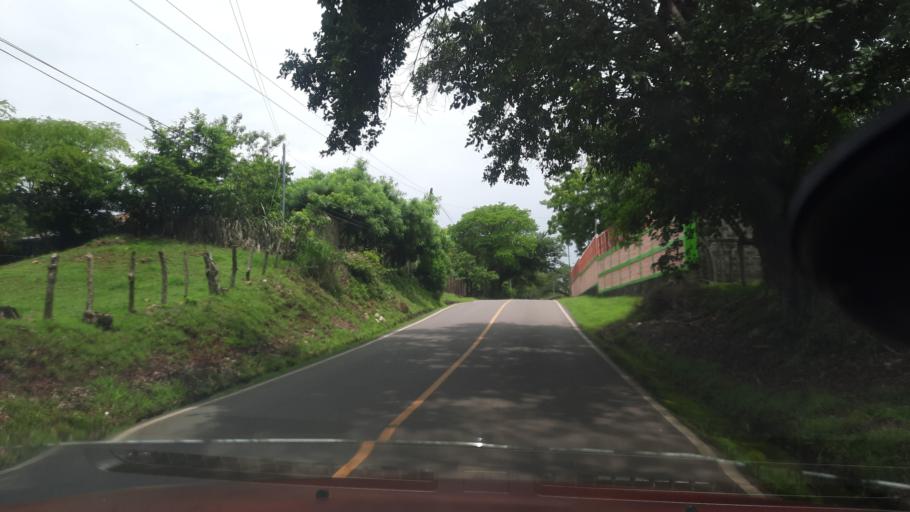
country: SV
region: La Union
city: Santa Rosa de Lima
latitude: 13.6473
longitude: -87.8533
